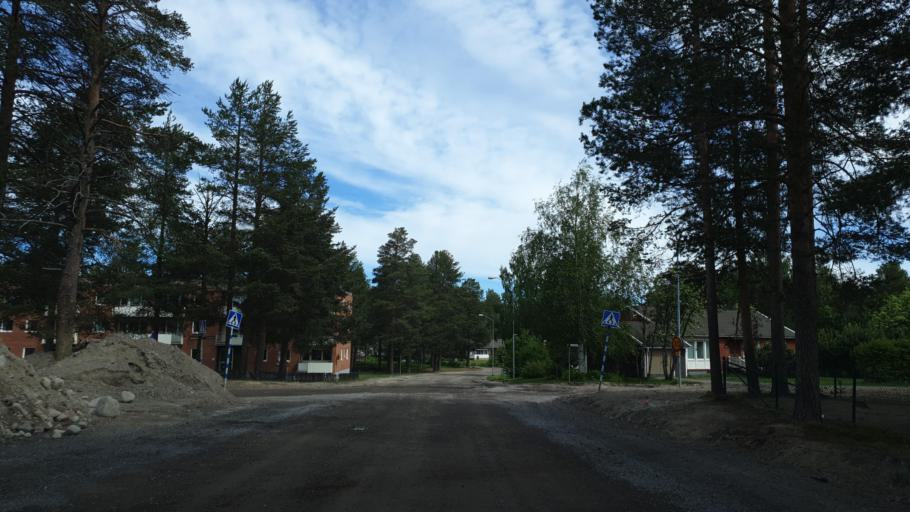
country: SE
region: Norrbotten
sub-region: Arvidsjaurs Kommun
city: Arvidsjaur
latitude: 65.5922
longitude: 19.1824
